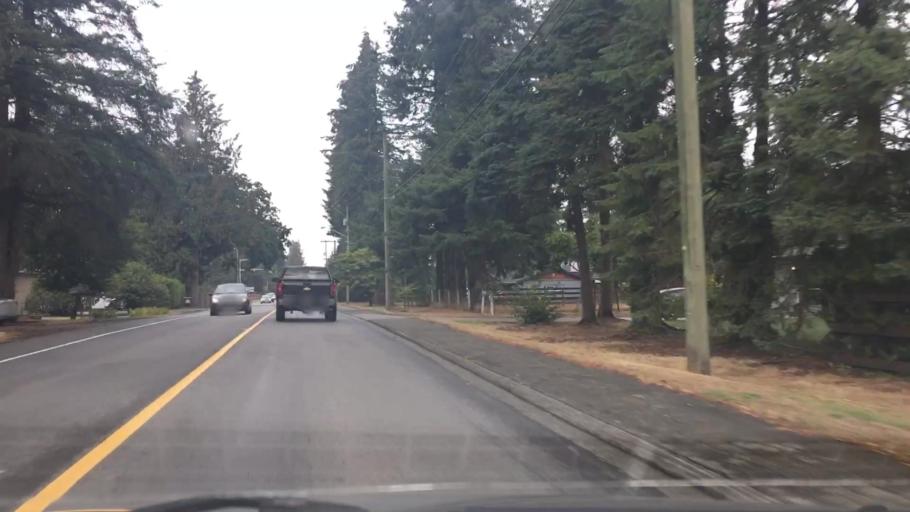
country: CA
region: British Columbia
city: Langley
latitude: 49.1040
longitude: -122.5342
